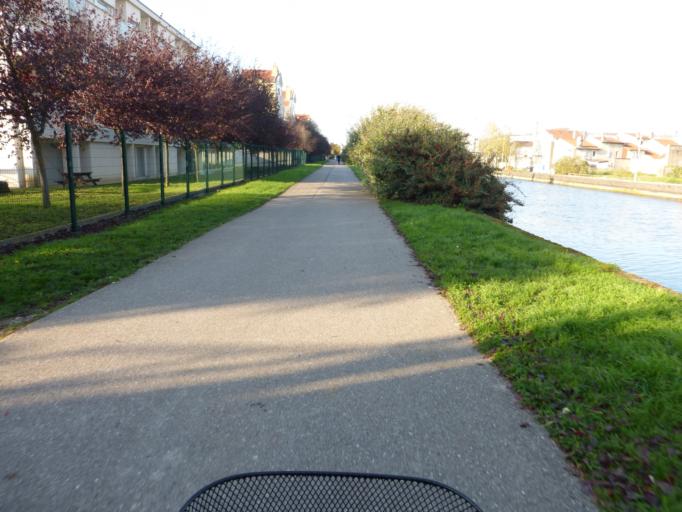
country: FR
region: Lorraine
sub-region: Departement de Meurthe-et-Moselle
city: Nancy
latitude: 48.6875
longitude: 6.1966
